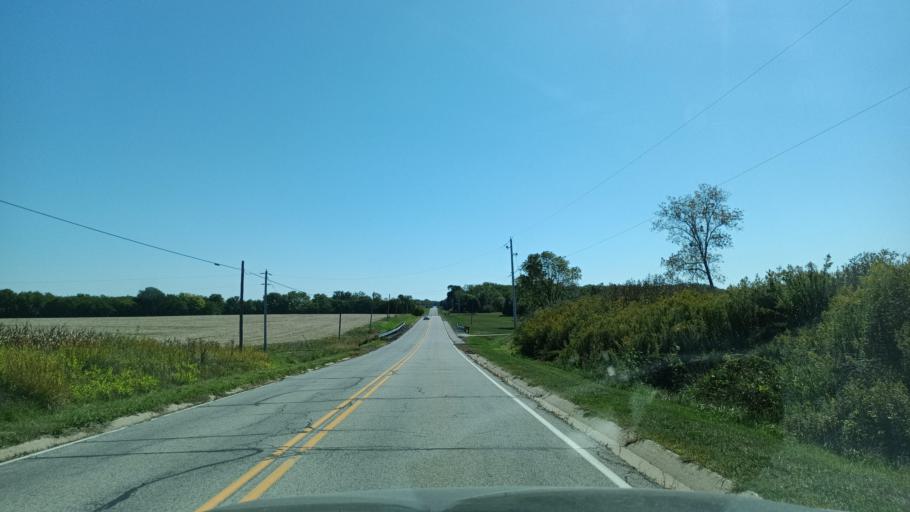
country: US
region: Illinois
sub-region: Peoria County
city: Elmwood
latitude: 40.8493
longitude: -89.9138
